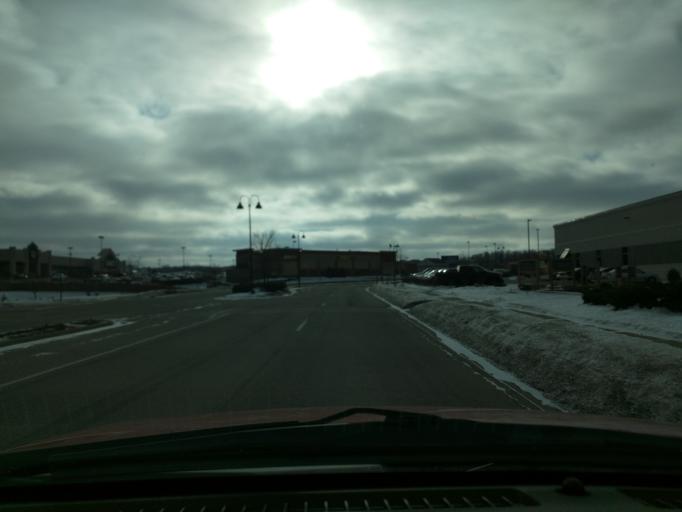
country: US
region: Minnesota
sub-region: Olmsted County
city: Rochester
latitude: 43.9569
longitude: -92.4614
